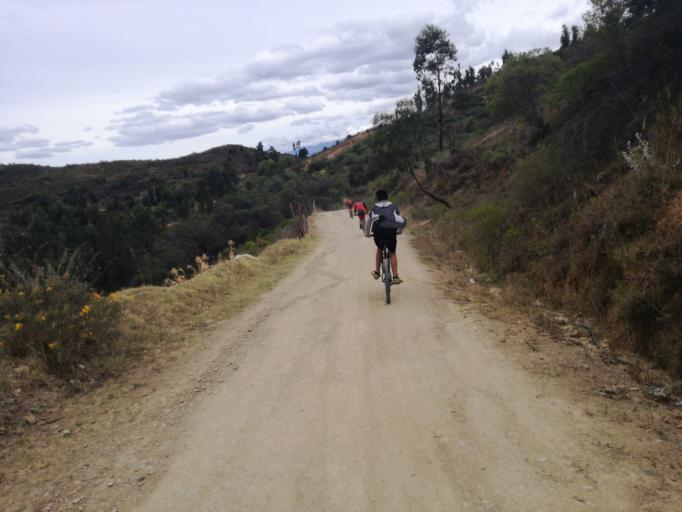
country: CO
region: Boyaca
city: Socha Viejo
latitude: 6.0098
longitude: -72.6847
